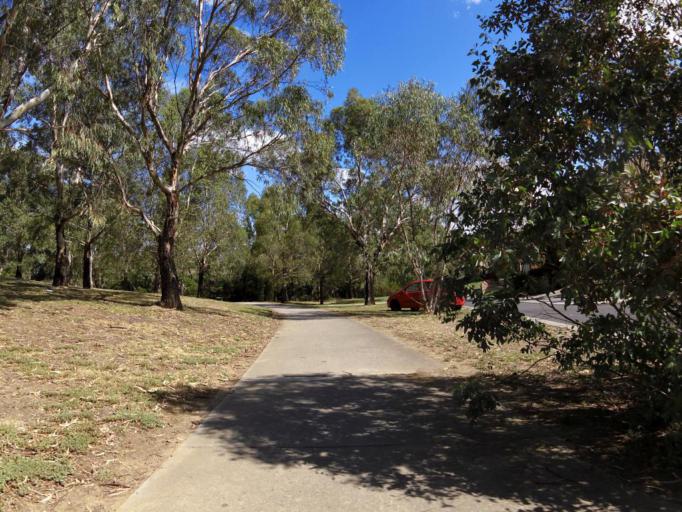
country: AU
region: Victoria
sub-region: Hume
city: Westmeadows
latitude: -37.6739
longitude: 144.8919
